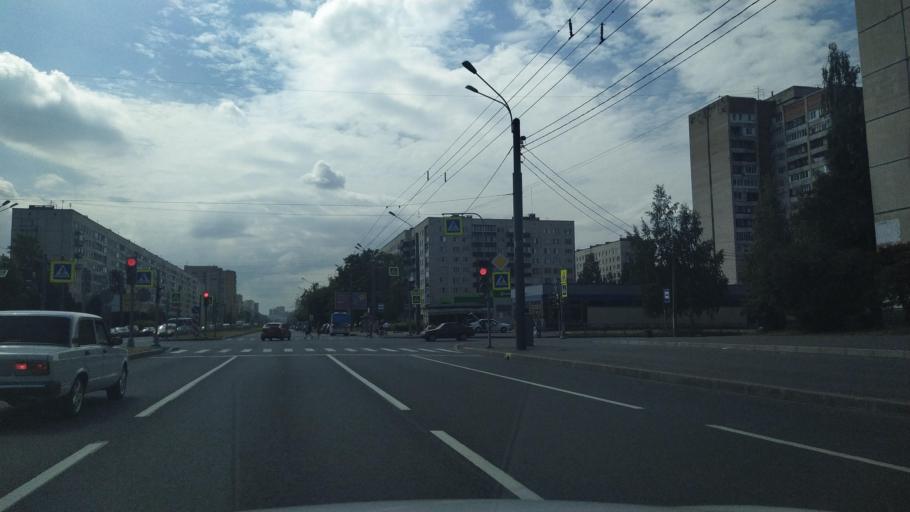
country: RU
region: Leningrad
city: Parnas
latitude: 60.0534
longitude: 30.3577
